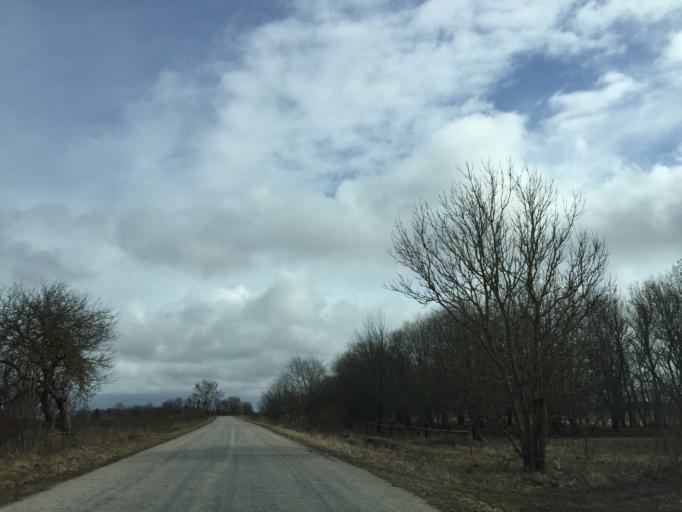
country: EE
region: Laeaene
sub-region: Lihula vald
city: Lihula
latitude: 58.7359
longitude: 23.8382
